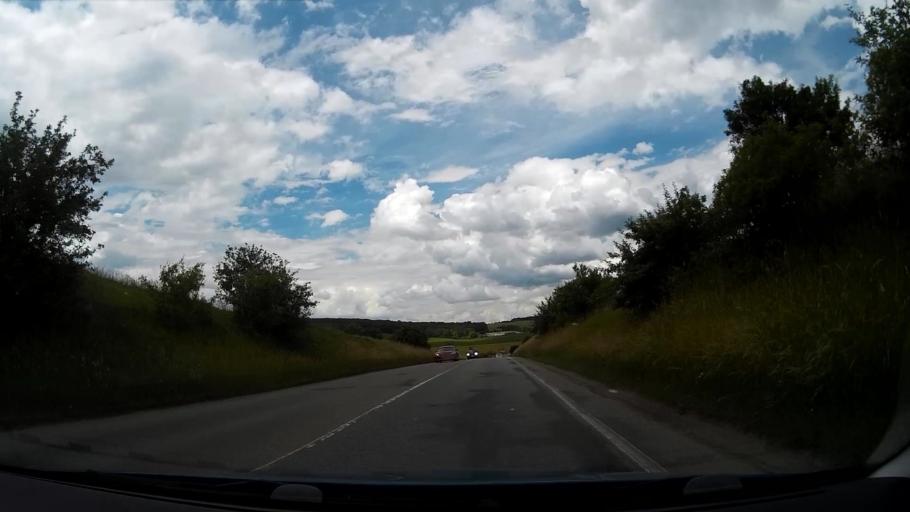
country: CZ
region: South Moravian
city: Troubsko
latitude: 49.1797
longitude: 16.5047
